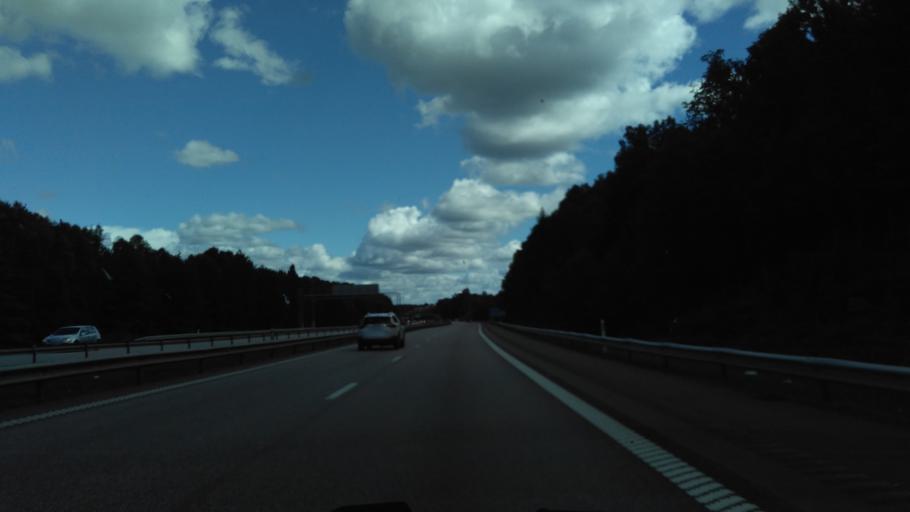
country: SE
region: Vaestra Goetaland
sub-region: Molndal
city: Moelndal
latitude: 57.6746
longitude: 12.0635
